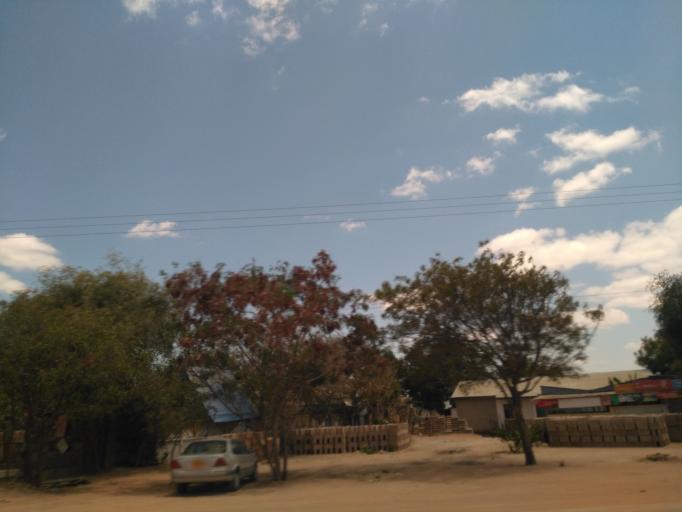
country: TZ
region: Dodoma
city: Kisasa
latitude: -6.1634
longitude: 35.7886
